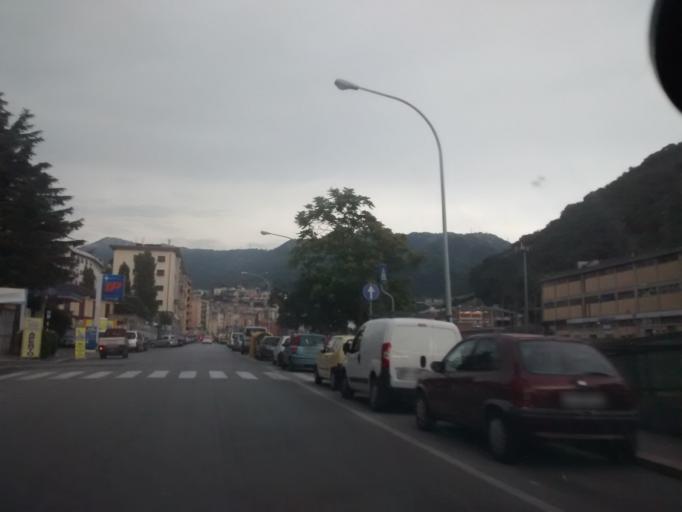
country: IT
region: Liguria
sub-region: Provincia di Genova
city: Piccarello
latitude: 44.4495
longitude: 8.9724
